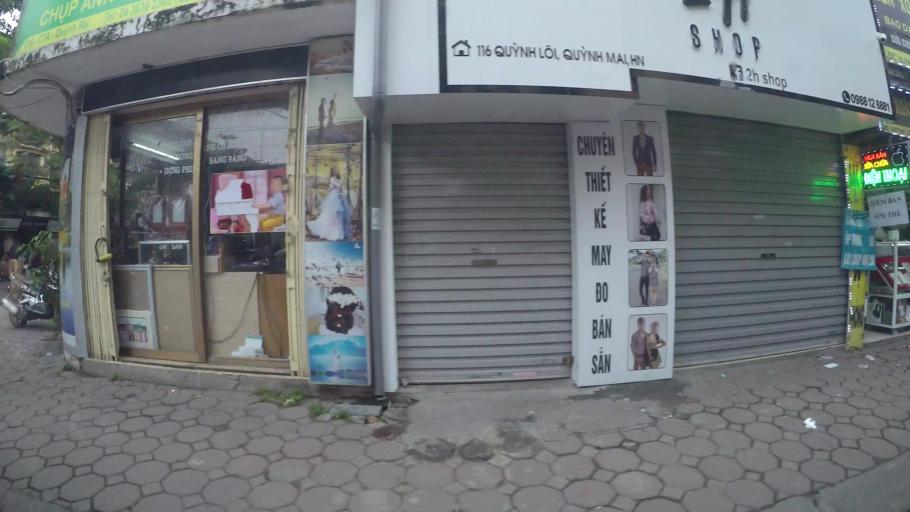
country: VN
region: Ha Noi
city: Hai BaTrung
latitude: 21.0011
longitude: 105.8598
